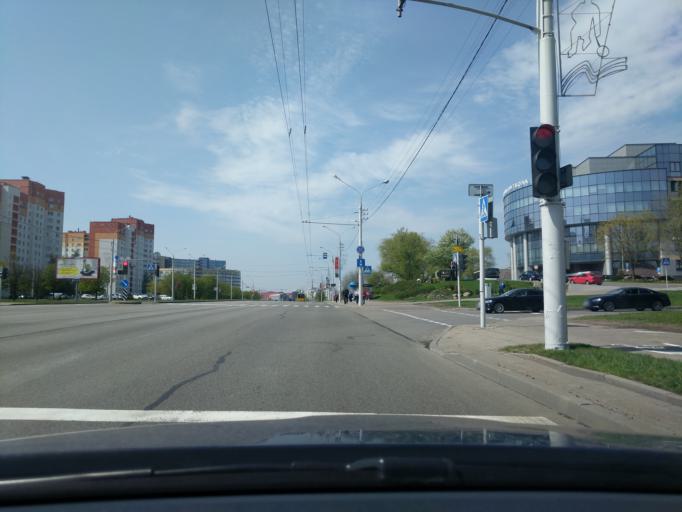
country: BY
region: Minsk
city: Minsk
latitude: 53.9340
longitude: 27.5029
